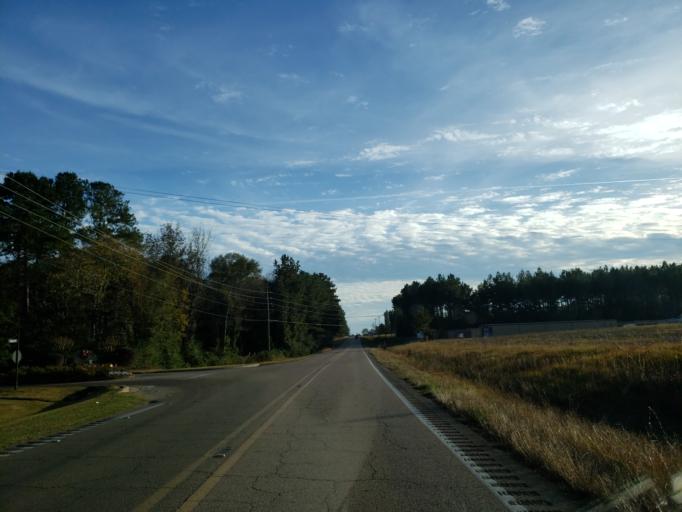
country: US
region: Mississippi
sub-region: Lamar County
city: West Hattiesburg
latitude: 31.2769
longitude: -89.4656
